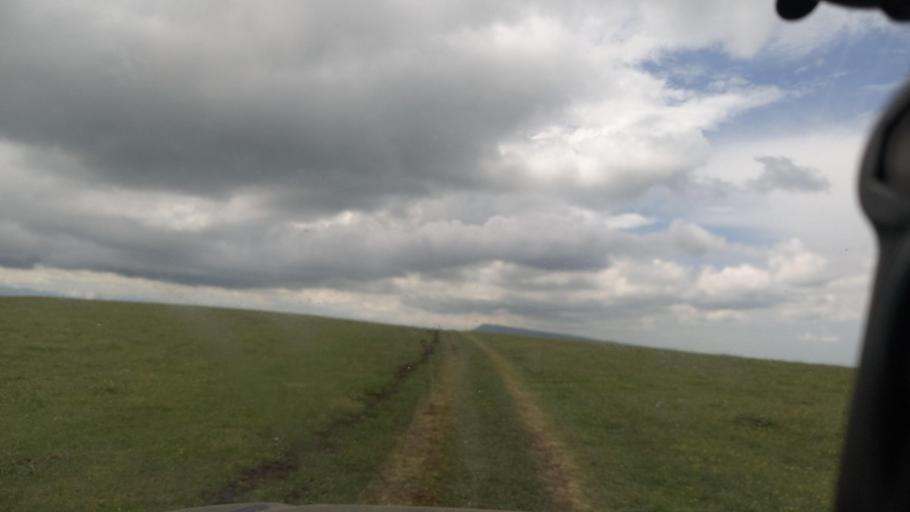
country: RU
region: Karachayevo-Cherkesiya
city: Pregradnaya
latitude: 43.9907
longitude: 41.2791
